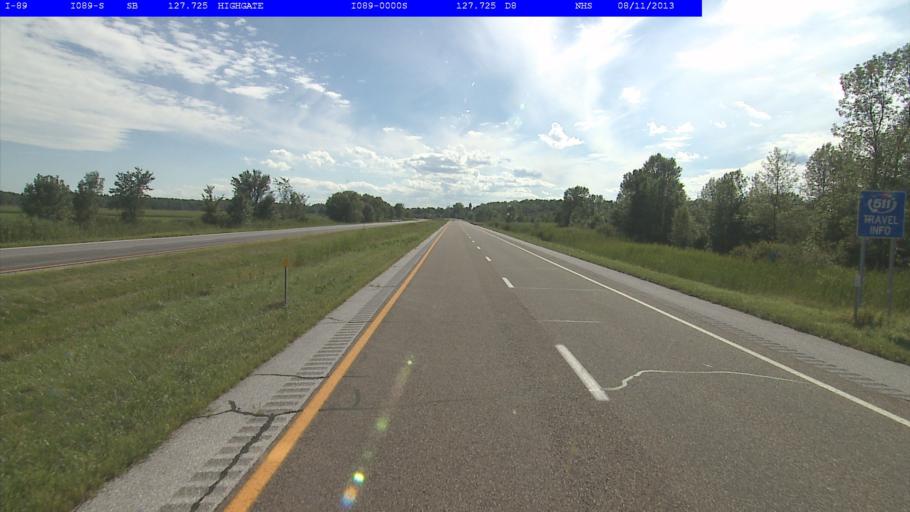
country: US
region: Vermont
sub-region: Franklin County
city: Swanton
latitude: 44.9814
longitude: -73.0954
